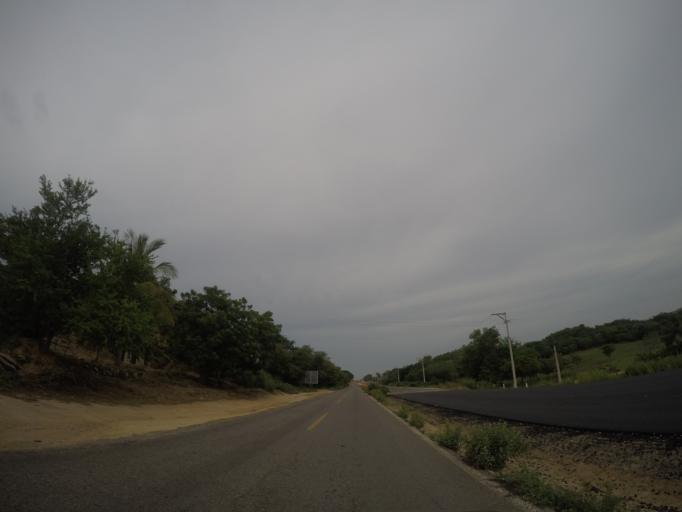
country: MX
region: Oaxaca
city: Santa Maria Tonameca
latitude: 15.7229
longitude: -96.6173
